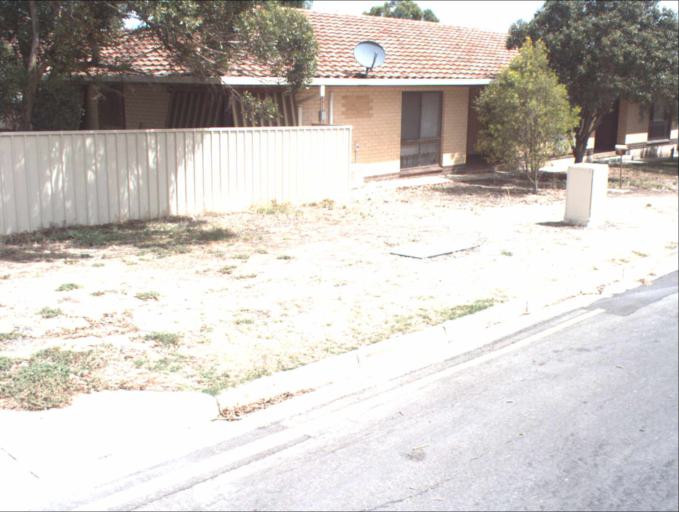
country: AU
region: South Australia
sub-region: Port Adelaide Enfield
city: Gilles Plains
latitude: -34.8420
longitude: 138.6627
